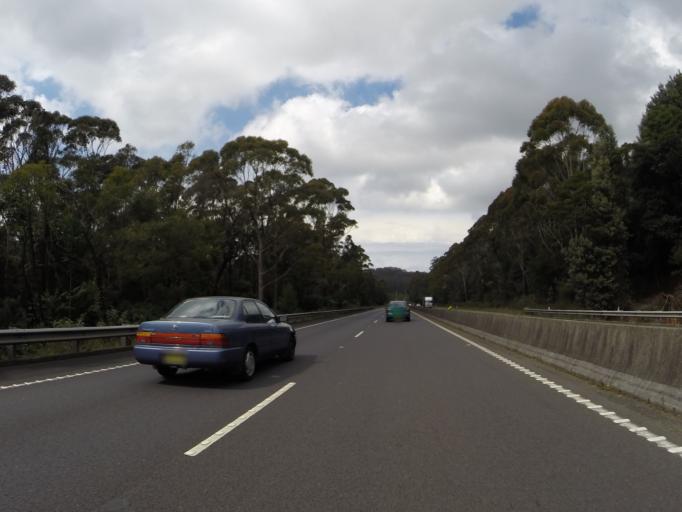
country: AU
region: New South Wales
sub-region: Wollongong
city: Bulli
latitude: -34.3309
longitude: 150.8778
